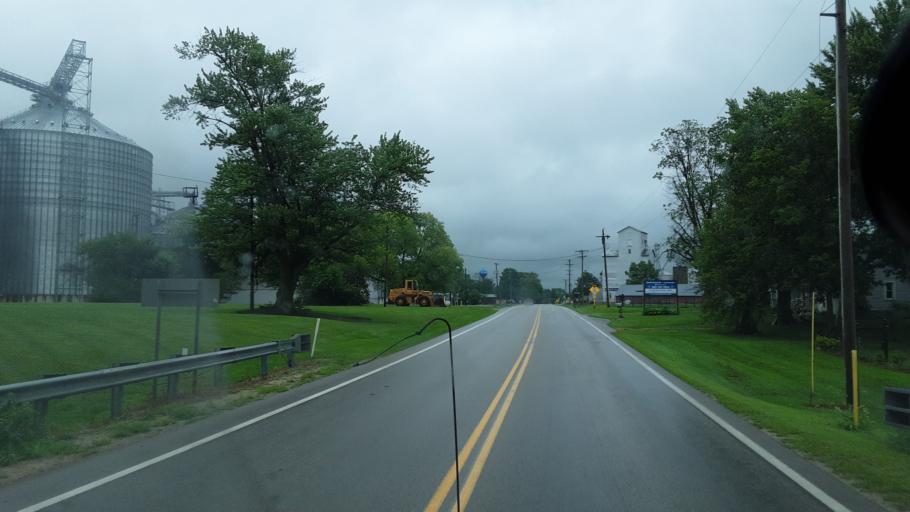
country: US
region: Indiana
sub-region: Adams County
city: Decatur
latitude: 40.7514
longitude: -84.8004
